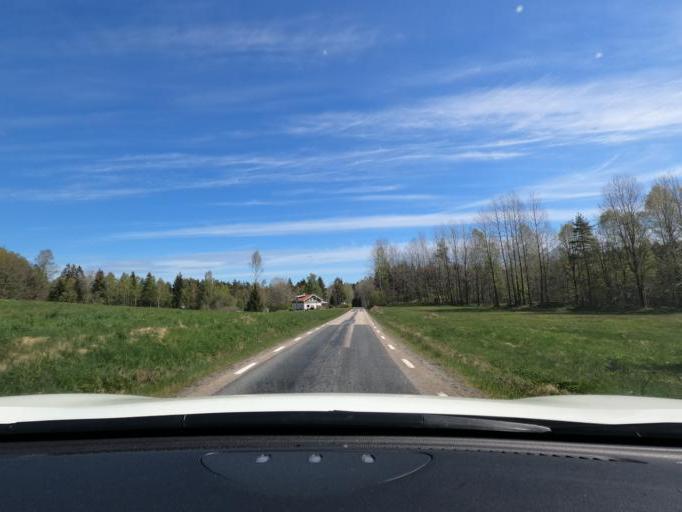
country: SE
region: Vaestra Goetaland
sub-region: Marks Kommun
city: Horred
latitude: 57.4369
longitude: 12.4190
